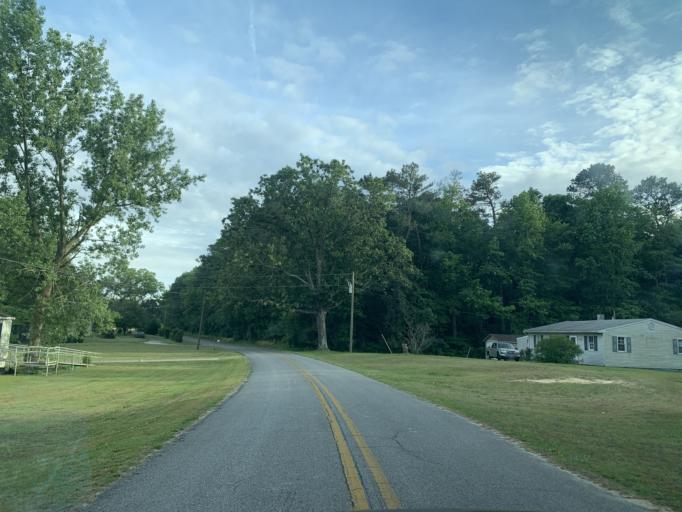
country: US
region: Maryland
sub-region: Worcester County
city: Pocomoke City
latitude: 38.0793
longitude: -75.4776
